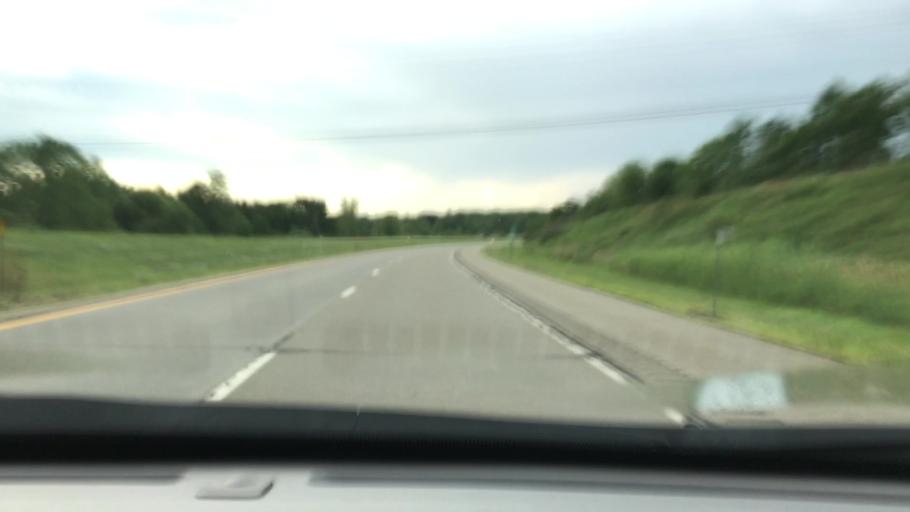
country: US
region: New York
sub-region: Erie County
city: North Boston
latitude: 42.6825
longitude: -78.7866
